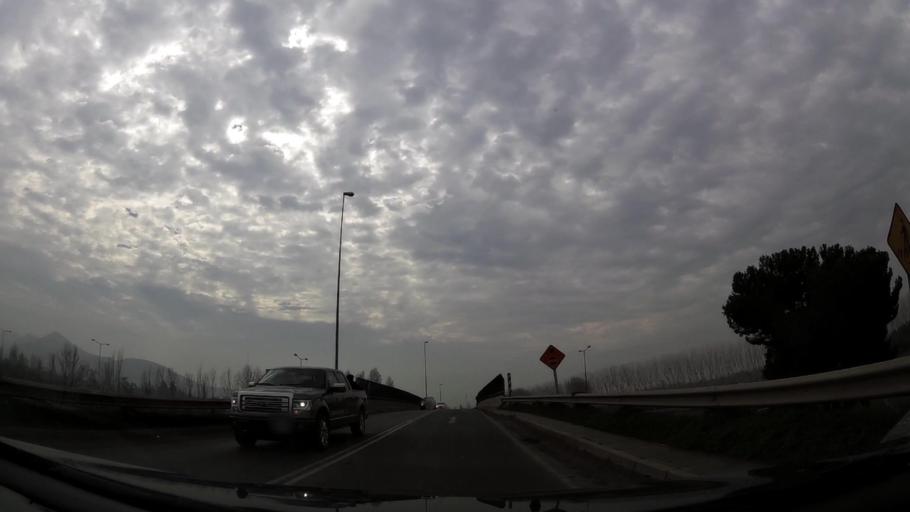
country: CL
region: Santiago Metropolitan
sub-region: Provincia de Chacabuco
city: Chicureo Abajo
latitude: -33.2406
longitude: -70.7572
